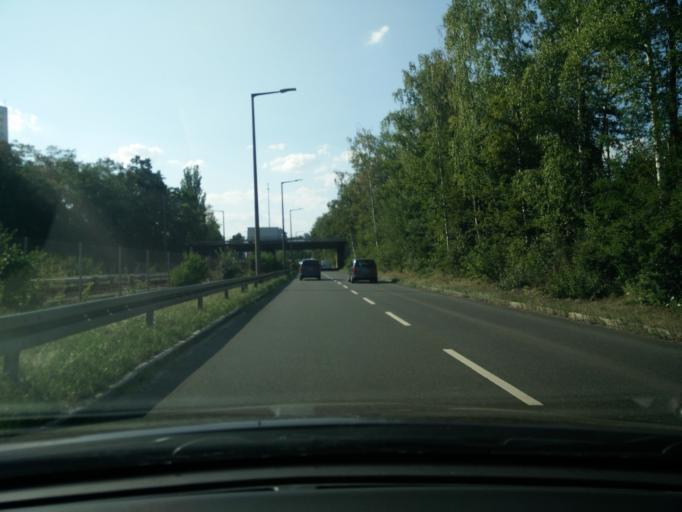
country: DE
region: Bavaria
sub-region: Regierungsbezirk Mittelfranken
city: Nuernberg
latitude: 49.4140
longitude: 11.1199
